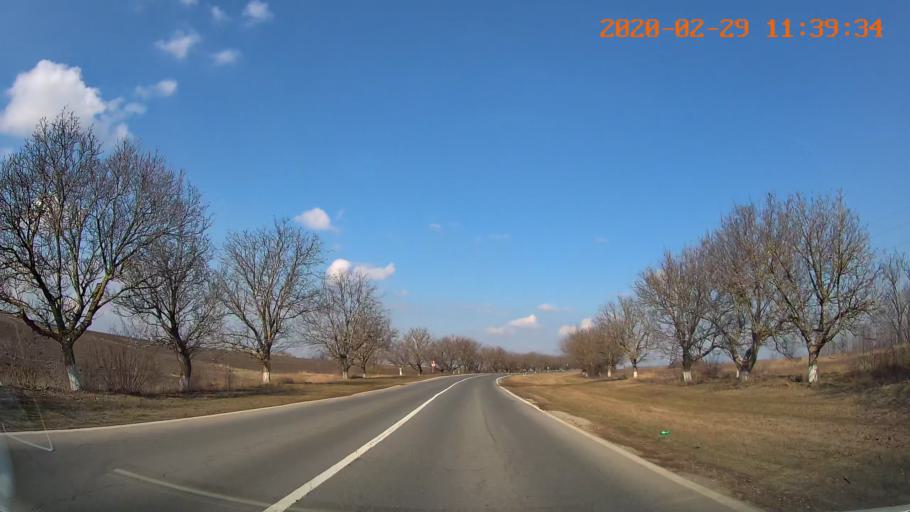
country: MD
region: Rezina
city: Saharna
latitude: 47.6421
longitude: 29.0240
